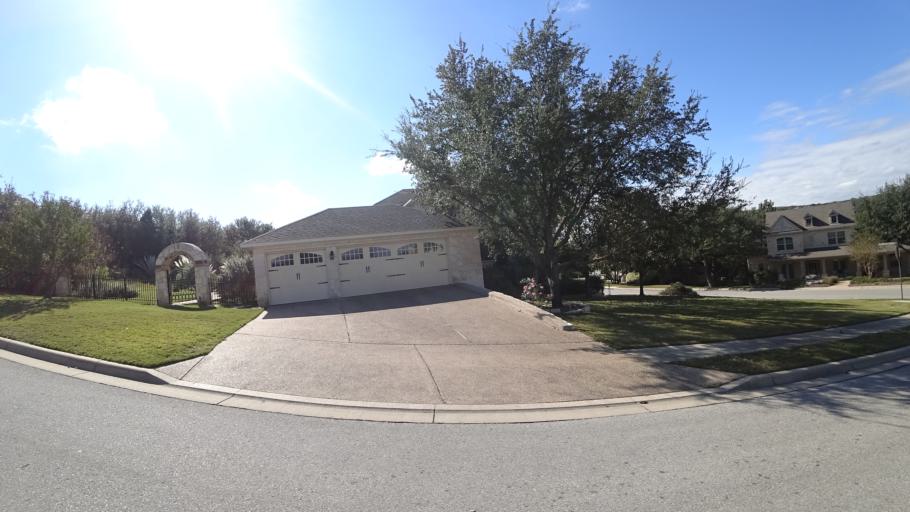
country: US
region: Texas
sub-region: Travis County
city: Hudson Bend
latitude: 30.3791
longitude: -97.9097
